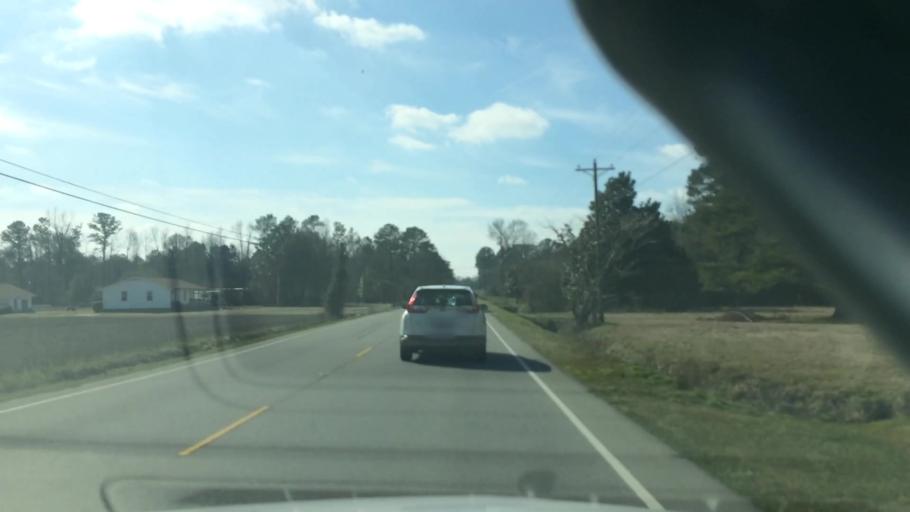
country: US
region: North Carolina
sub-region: Duplin County
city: Wallace
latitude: 34.7714
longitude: -77.9232
